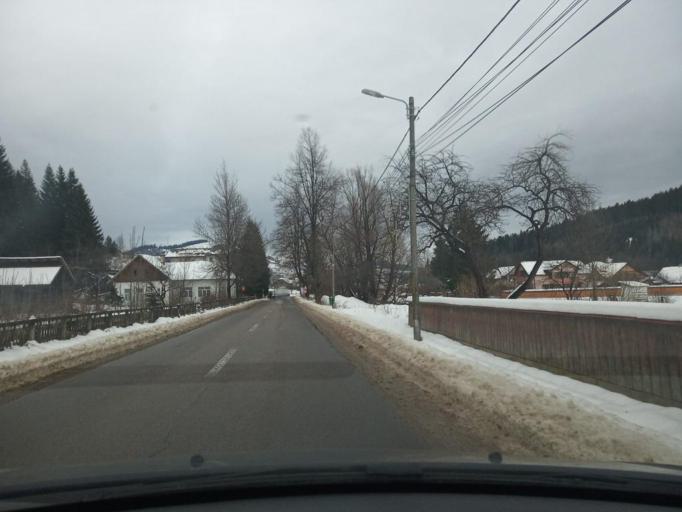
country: RO
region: Suceava
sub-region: Oras Gura Humorului
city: Gura Humorului
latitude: 47.5291
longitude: 25.8637
